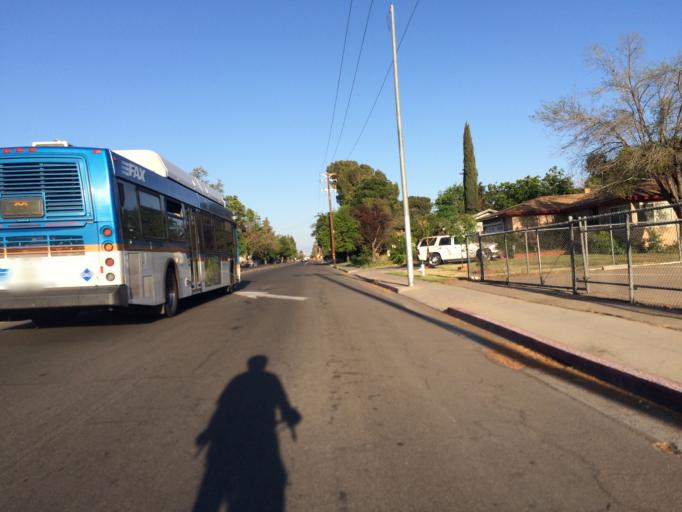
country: US
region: California
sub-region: Fresno County
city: Fresno
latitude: 36.7868
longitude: -119.7796
